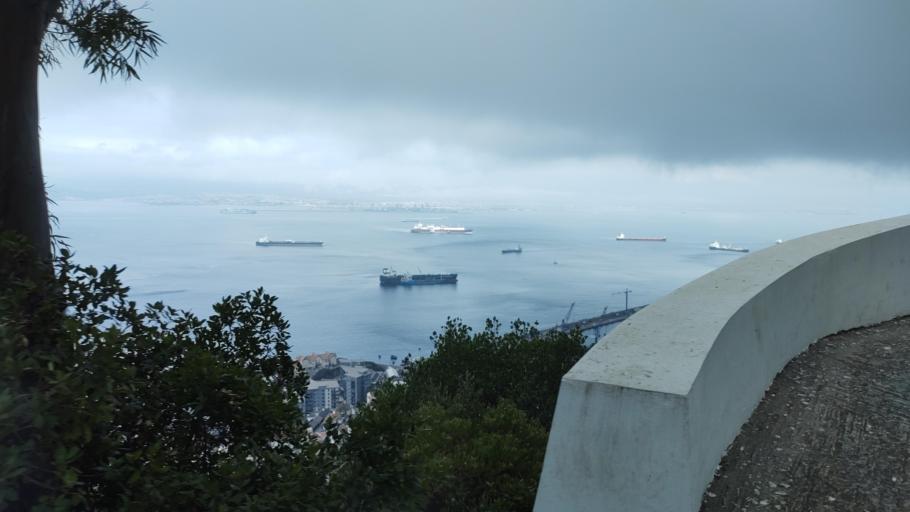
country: GI
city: Gibraltar
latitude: 36.1234
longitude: -5.3465
